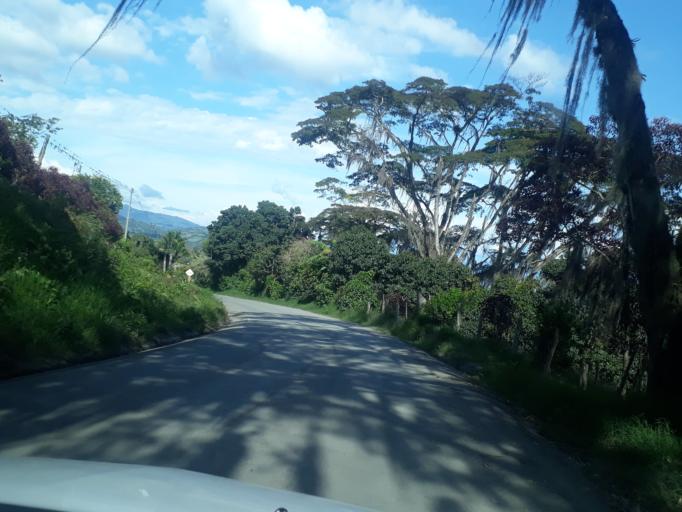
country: CO
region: Santander
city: Velez
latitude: 6.0425
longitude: -73.6525
